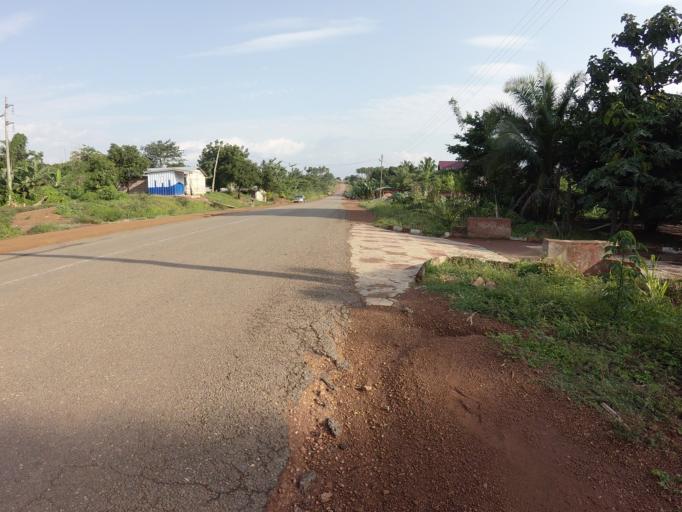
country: GH
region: Volta
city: Hohoe
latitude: 7.0520
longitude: 0.4272
